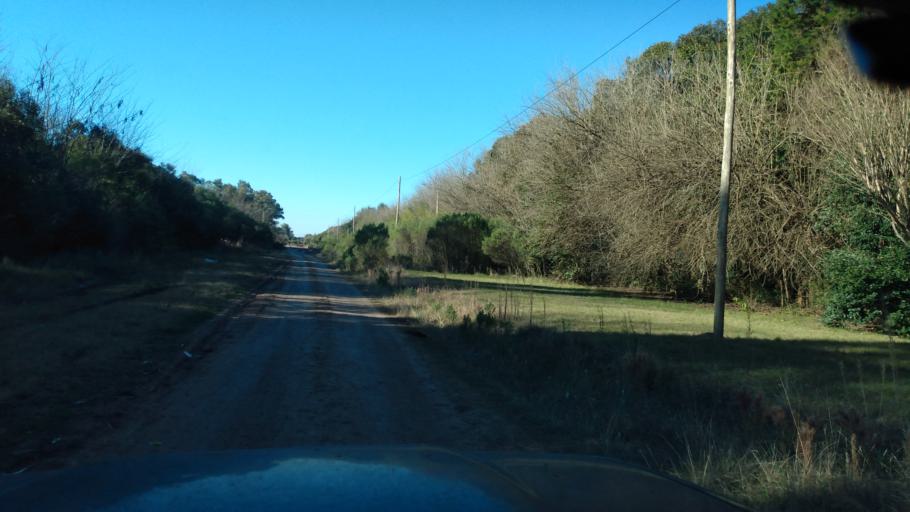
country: AR
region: Buenos Aires
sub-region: Partido de Lujan
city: Lujan
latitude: -34.5555
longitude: -59.1513
